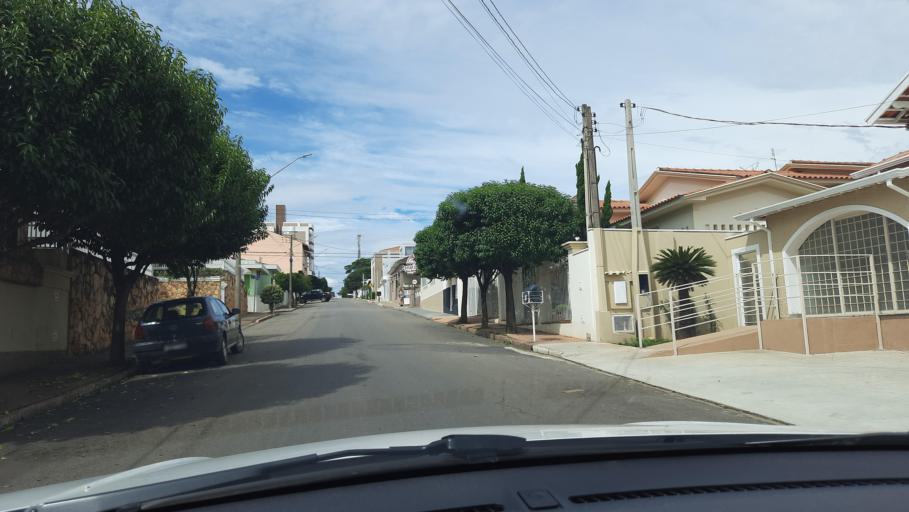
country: BR
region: Sao Paulo
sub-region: Vargem Grande Do Sul
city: Vargem Grande do Sul
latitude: -21.8325
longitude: -46.8916
